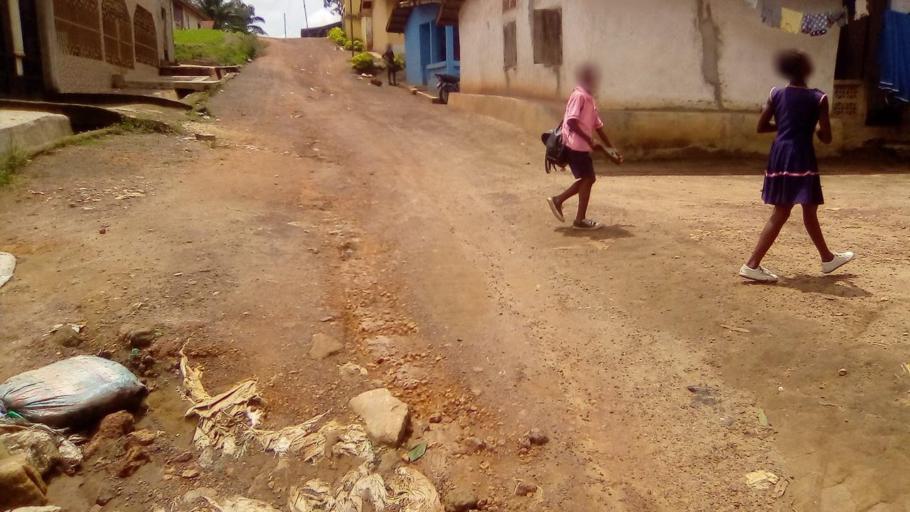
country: SL
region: Southern Province
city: Bo
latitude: 7.9358
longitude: -11.7346
